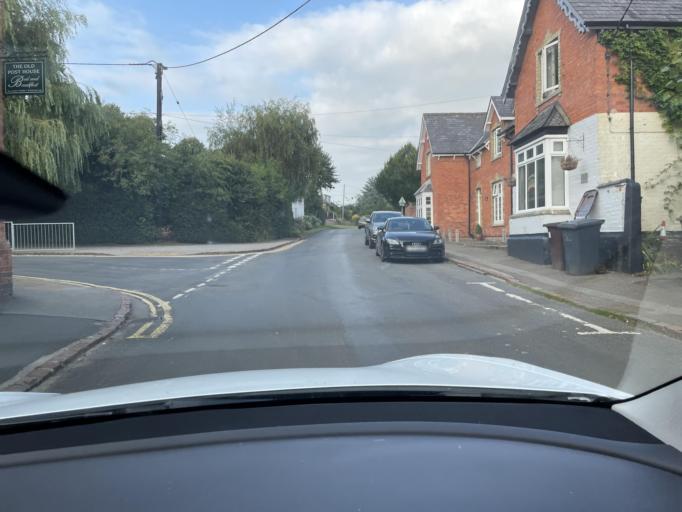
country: GB
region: England
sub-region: Leicestershire
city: Market Harborough
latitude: 52.3953
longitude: -0.9886
